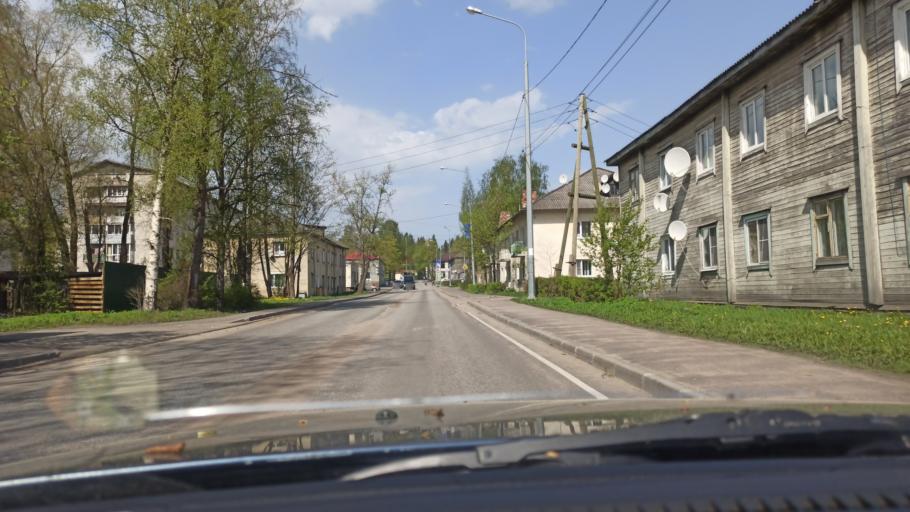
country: RU
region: Republic of Karelia
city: Lakhdenpokh'ya
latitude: 61.5181
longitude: 30.2015
